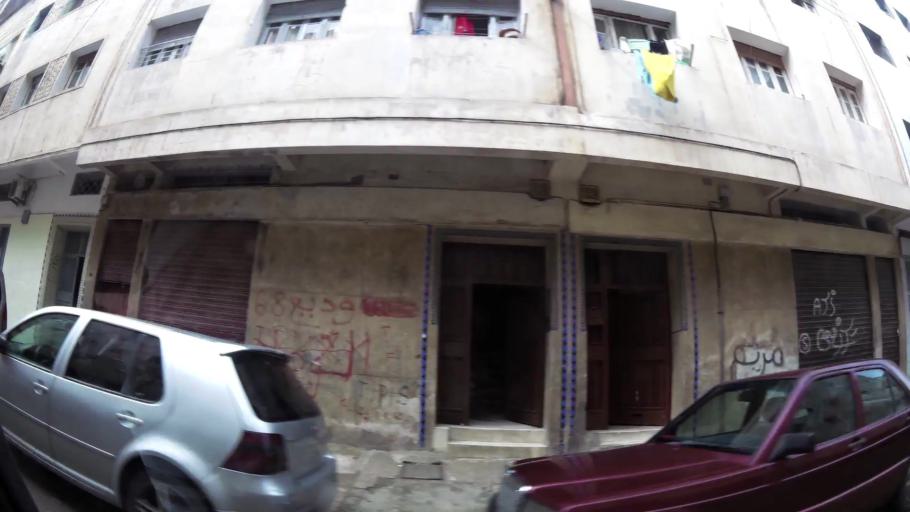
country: MA
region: Grand Casablanca
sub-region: Casablanca
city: Casablanca
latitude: 33.5709
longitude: -7.5897
